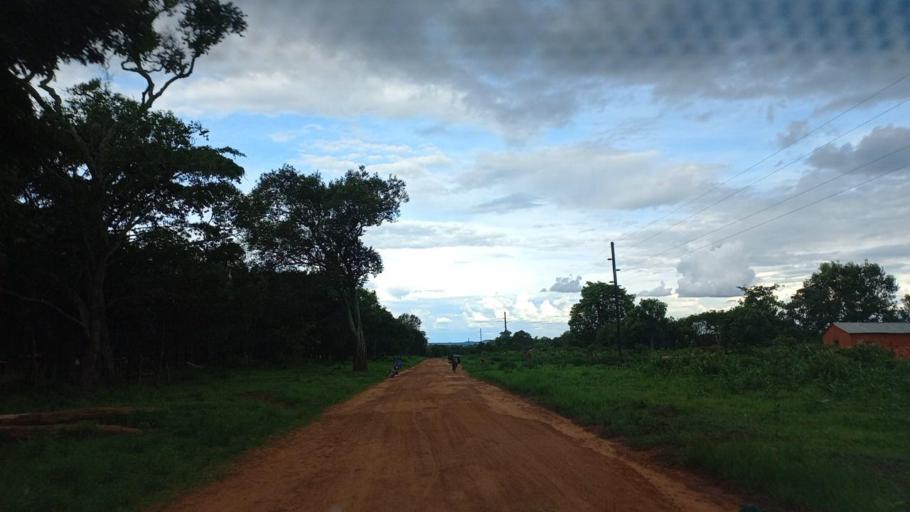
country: ZM
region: North-Western
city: Mwinilunga
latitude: -11.7750
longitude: 24.3898
